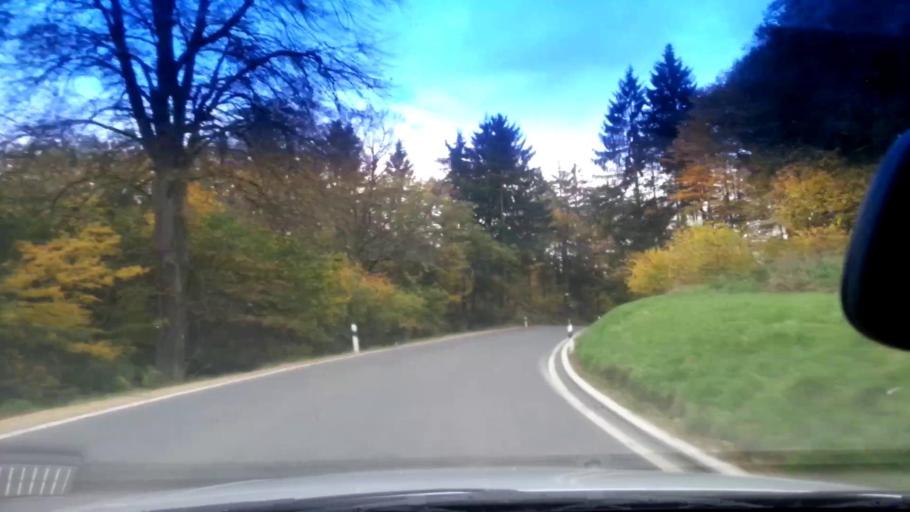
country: DE
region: Bavaria
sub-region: Upper Franconia
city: Wonsees
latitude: 49.9870
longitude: 11.2963
